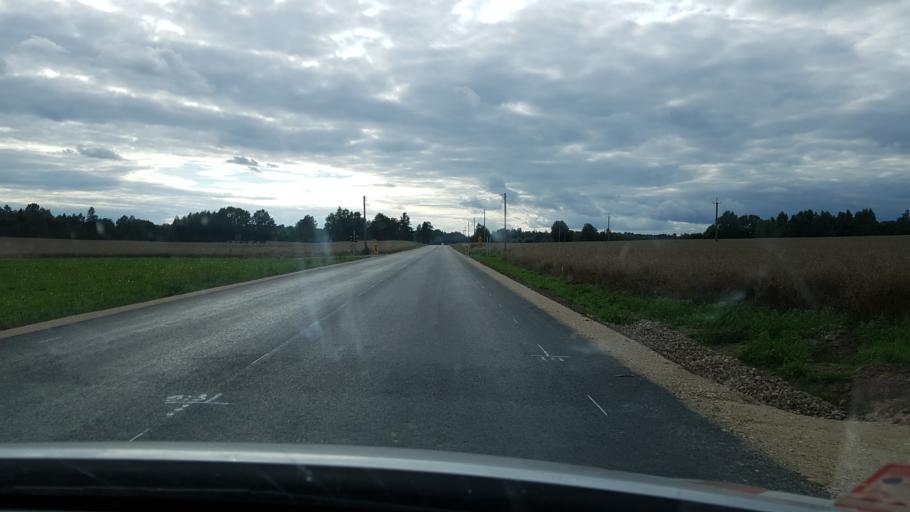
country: EE
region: Vorumaa
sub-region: Antsla vald
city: Vana-Antsla
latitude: 57.8802
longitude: 26.7111
